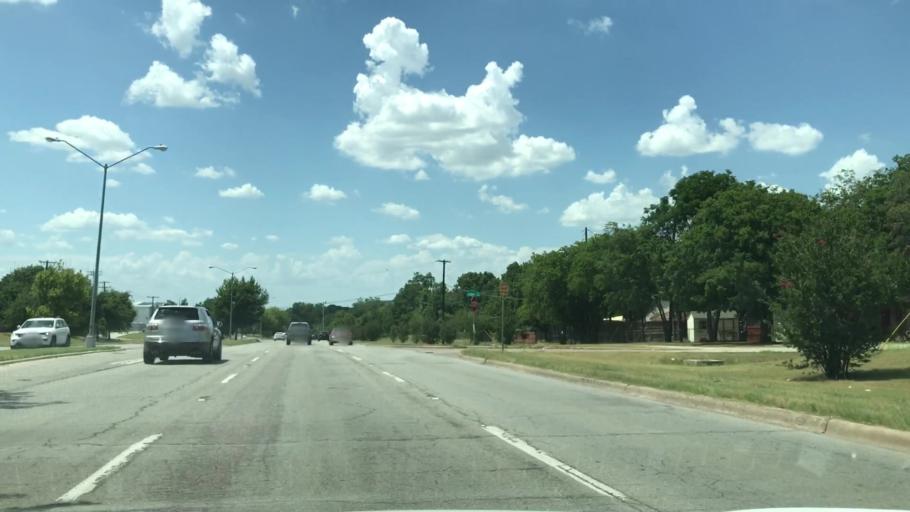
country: US
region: Texas
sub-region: Dallas County
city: University Park
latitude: 32.8554
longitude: -96.8465
